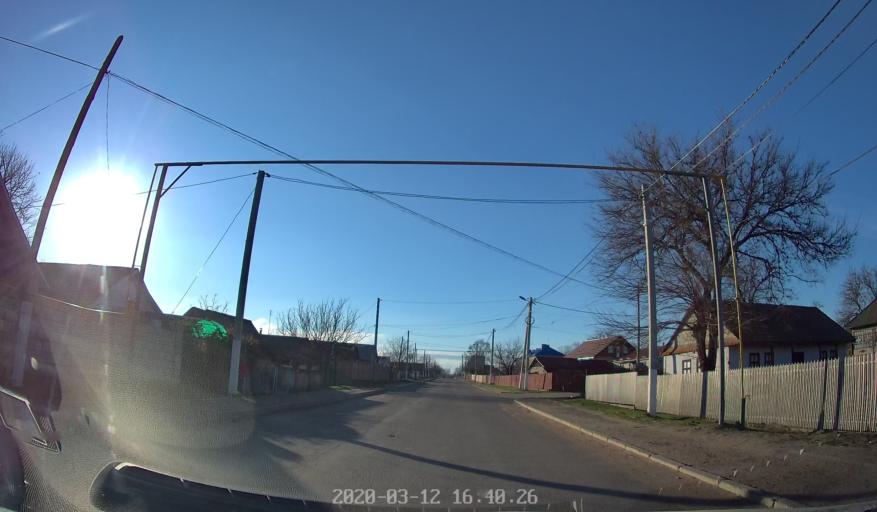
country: MD
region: Anenii Noi
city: Anenii Noi
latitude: 46.8180
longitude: 29.1481
